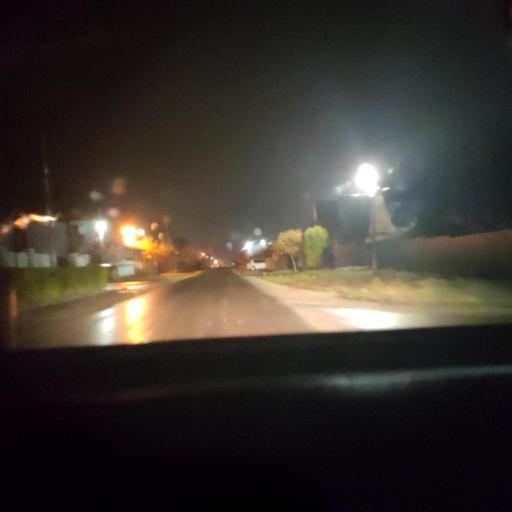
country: RU
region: Voronezj
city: Semiluki
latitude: 51.7082
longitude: 39.0271
